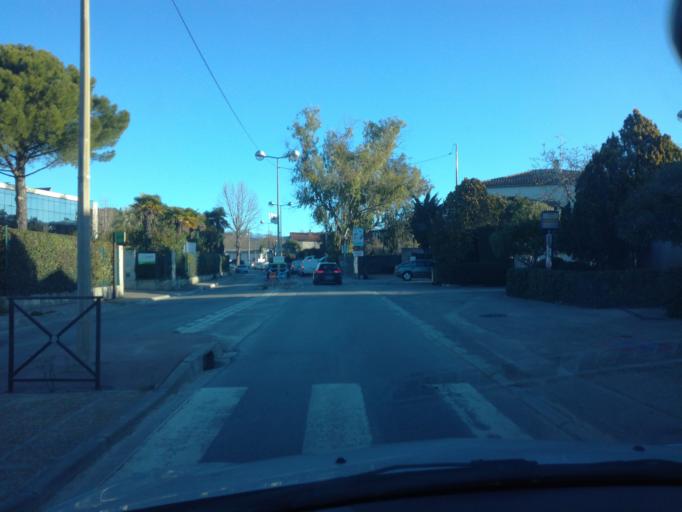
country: FR
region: Provence-Alpes-Cote d'Azur
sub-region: Departement des Alpes-Maritimes
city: La Roquette-sur-Siagne
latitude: 43.6055
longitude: 6.9716
